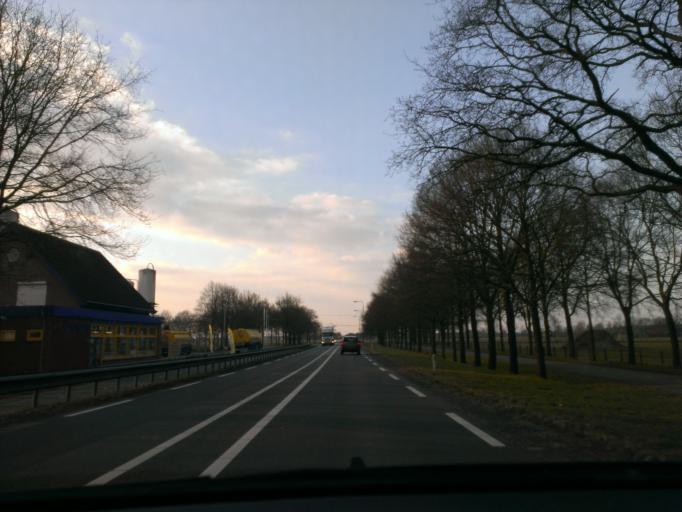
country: NL
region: Overijssel
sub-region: Gemeente Raalte
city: Heino
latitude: 52.4666
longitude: 6.2030
